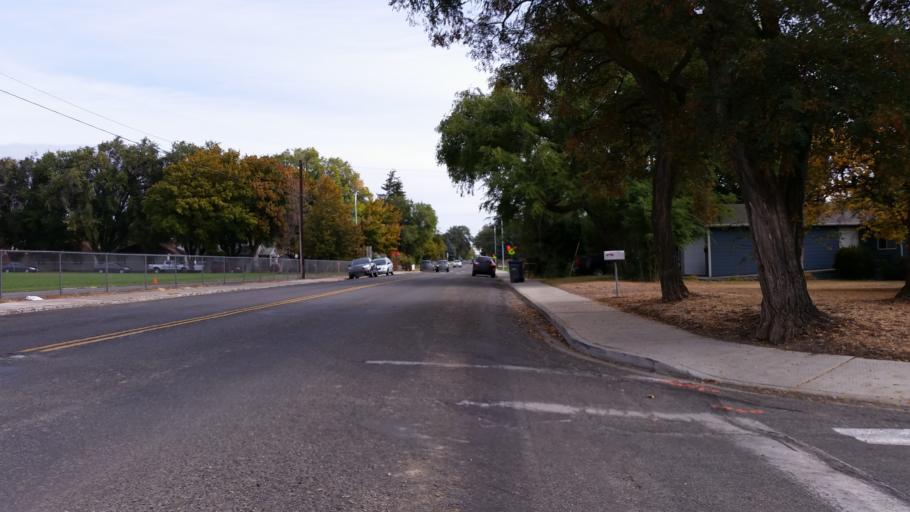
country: US
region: Washington
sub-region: Kittitas County
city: Ellensburg
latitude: 46.9914
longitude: -120.5417
